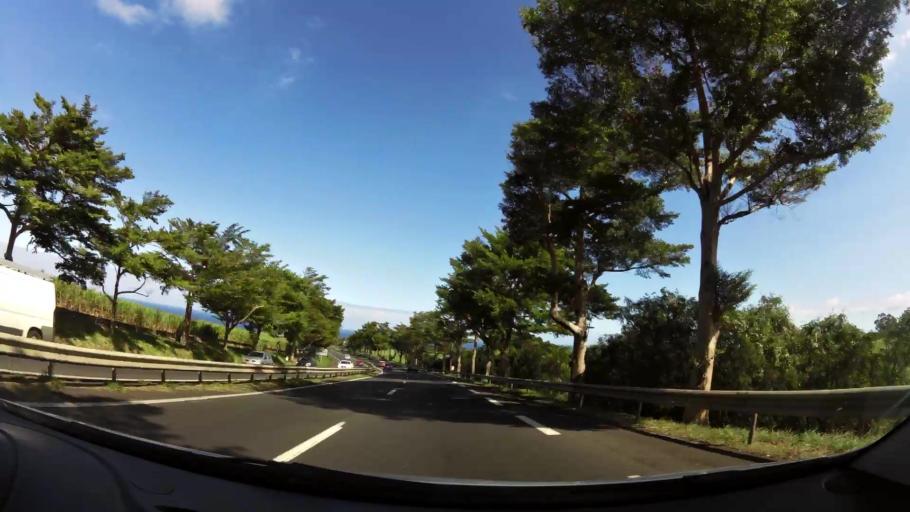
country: RE
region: Reunion
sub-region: Reunion
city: Saint-Pierre
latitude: -21.3165
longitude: 55.4911
